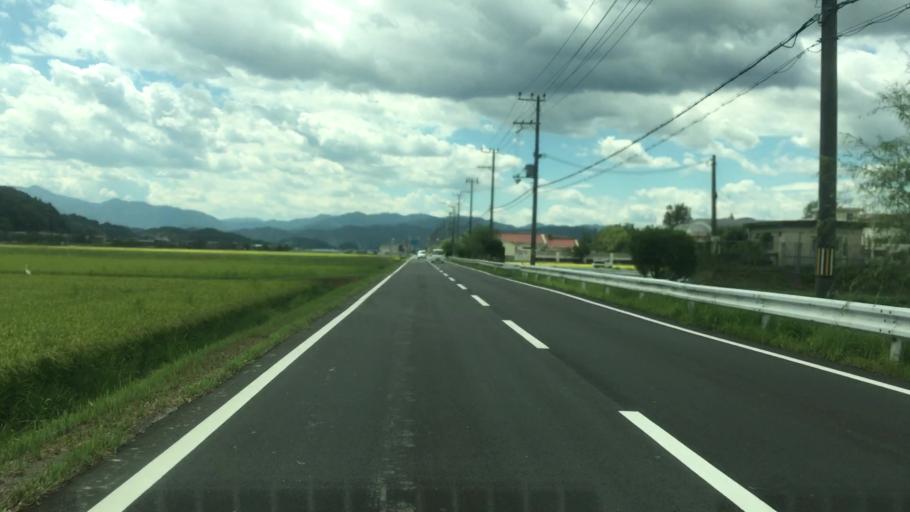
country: JP
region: Hyogo
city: Toyooka
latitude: 35.5324
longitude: 134.8397
